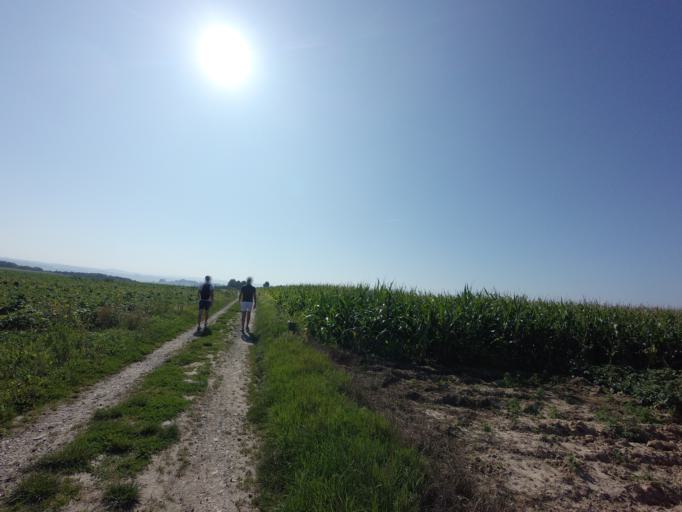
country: NL
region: Limburg
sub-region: Valkenburg aan de Geul
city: Schin op Geul
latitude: 50.8234
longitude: 5.8752
